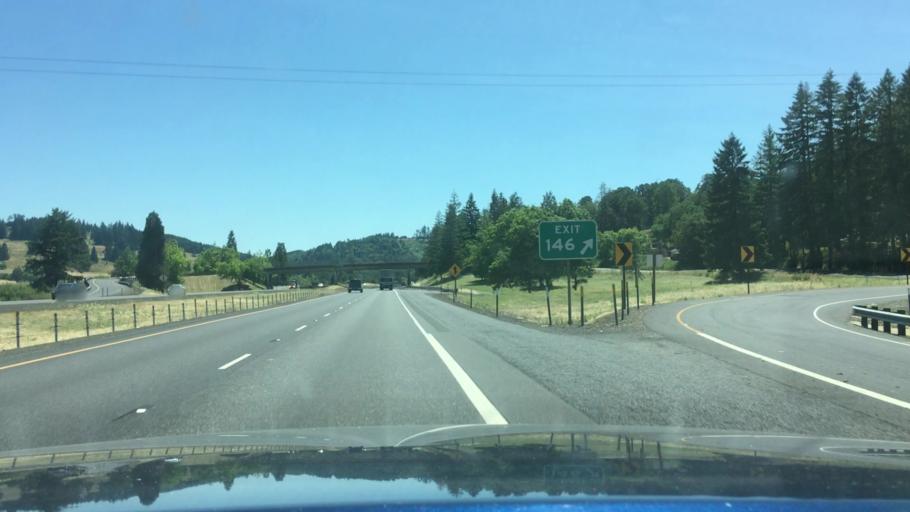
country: US
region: Oregon
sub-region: Douglas County
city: Yoncalla
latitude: 43.5158
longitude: -123.3147
